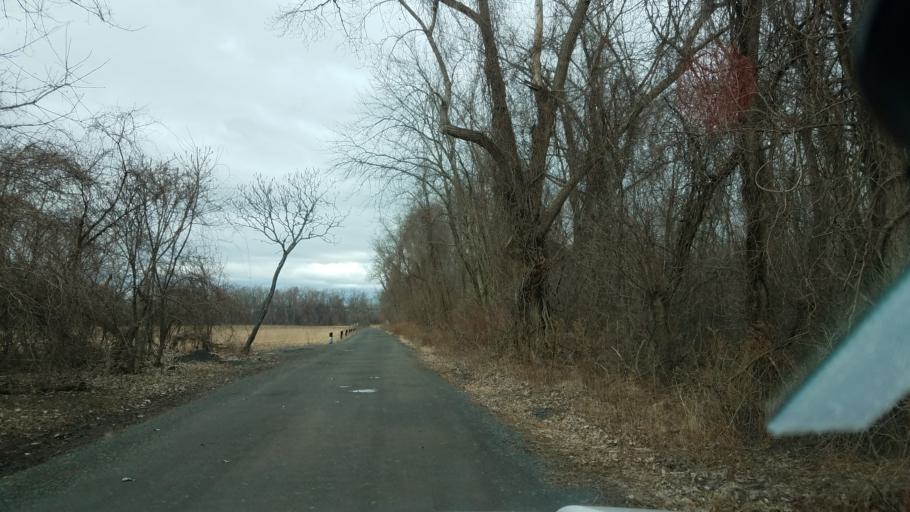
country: US
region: Connecticut
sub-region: Hartford County
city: Wethersfield
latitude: 41.7068
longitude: -72.6359
